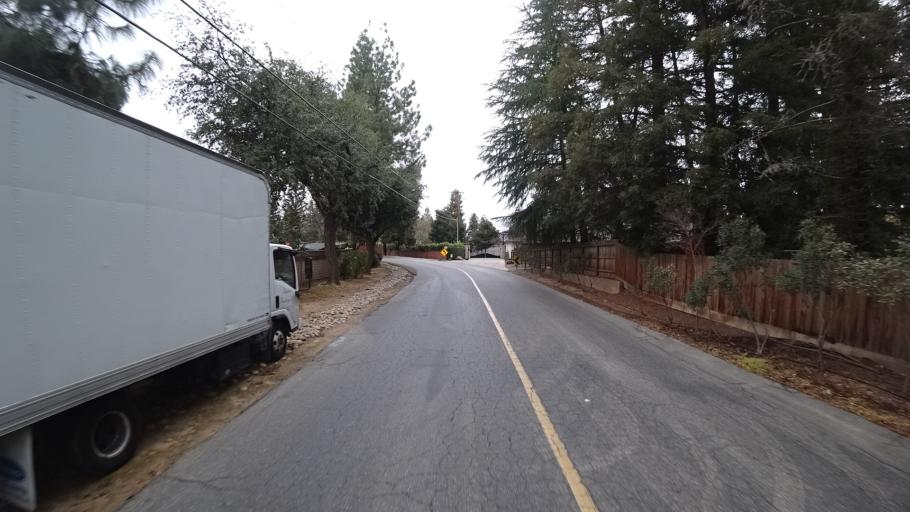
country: US
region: California
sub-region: Fresno County
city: Fresno
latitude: 36.8467
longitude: -119.8477
